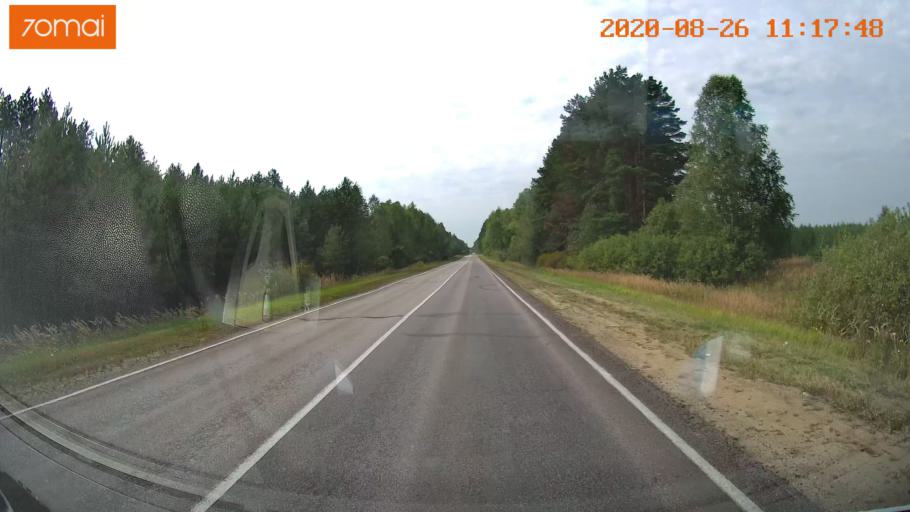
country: RU
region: Rjazan
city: Shilovo
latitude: 54.4157
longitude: 41.1073
